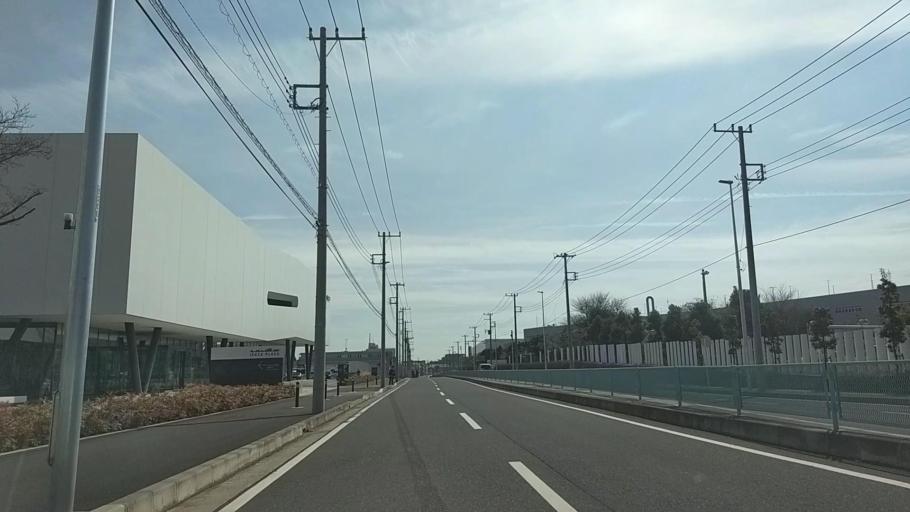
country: JP
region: Kanagawa
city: Fujisawa
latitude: 35.3996
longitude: 139.4562
